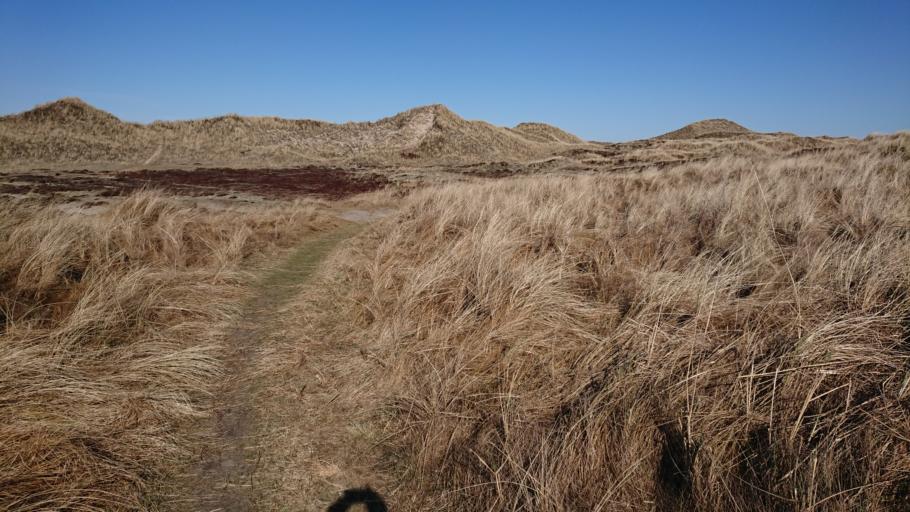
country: DK
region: North Denmark
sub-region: Frederikshavn Kommune
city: Strandby
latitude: 57.6371
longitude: 10.3426
